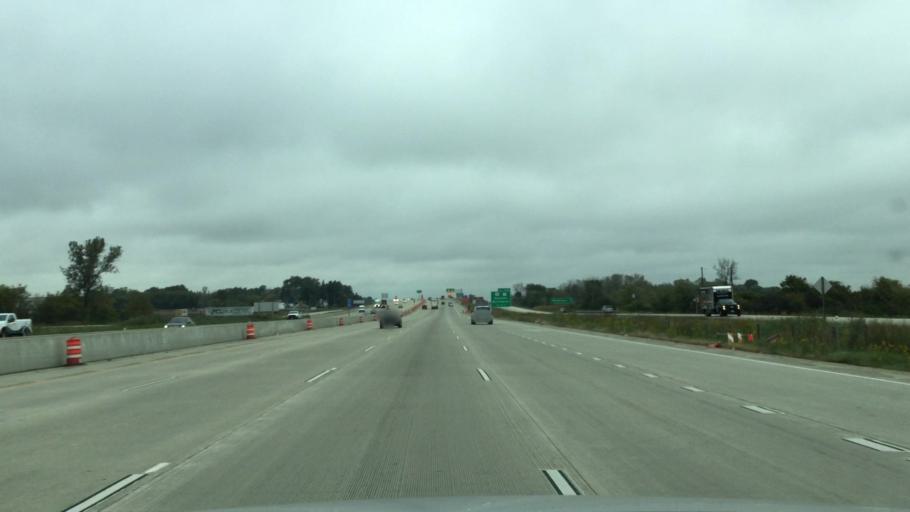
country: US
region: Wisconsin
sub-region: Kenosha County
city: Pleasant Prairie
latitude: 42.5952
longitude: -87.9524
